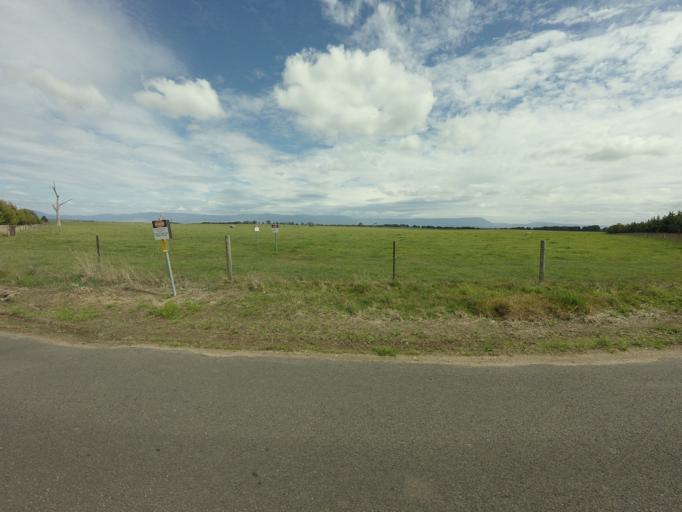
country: AU
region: Tasmania
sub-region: Northern Midlands
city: Longford
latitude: -41.6638
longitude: 147.1918
